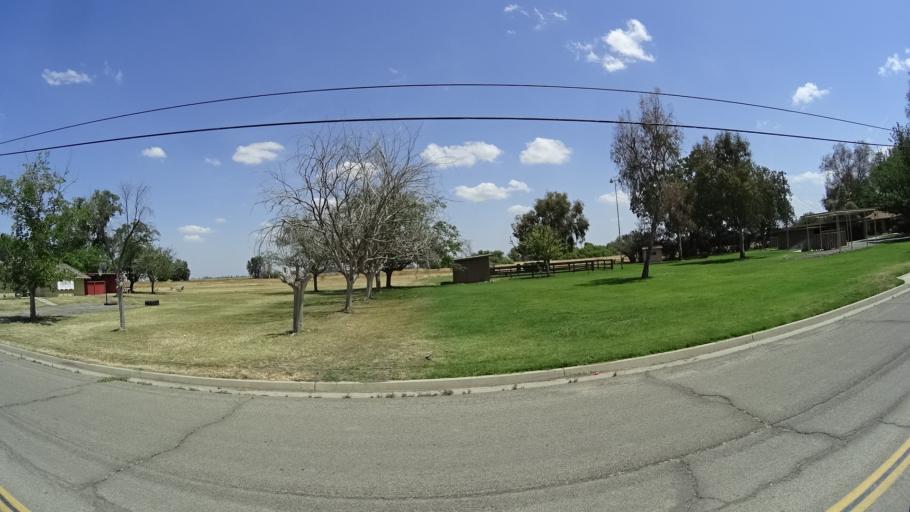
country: US
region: California
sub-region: Kings County
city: Stratford
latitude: 36.1943
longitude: -119.8206
